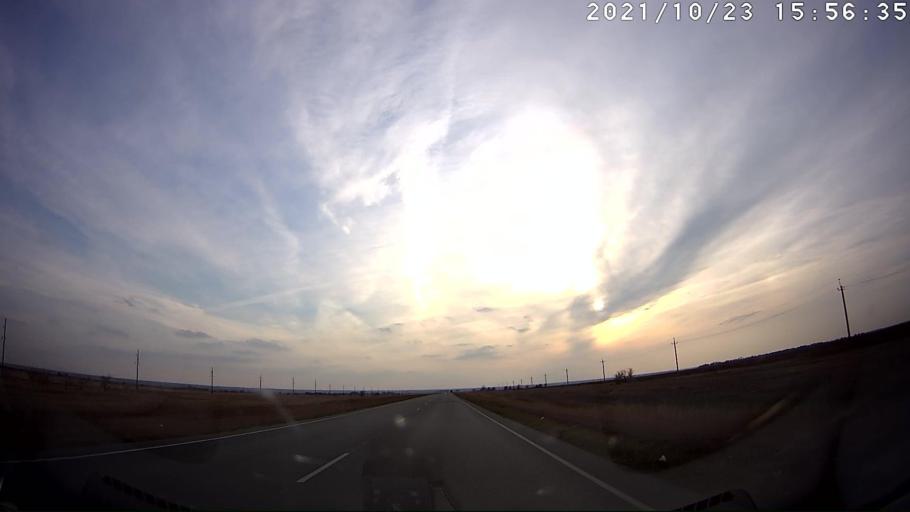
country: RU
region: Kalmykiya
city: Sadovoye
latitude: 47.9567
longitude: 43.9463
